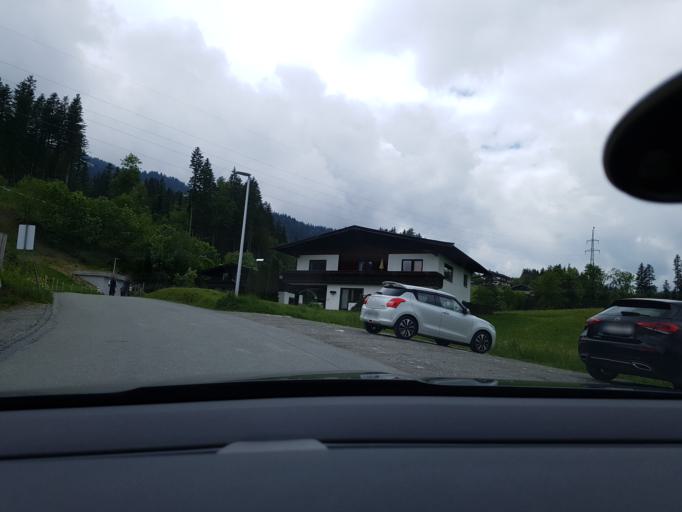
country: AT
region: Tyrol
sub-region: Politischer Bezirk Kufstein
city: Ellmau
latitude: 47.5124
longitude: 12.2898
